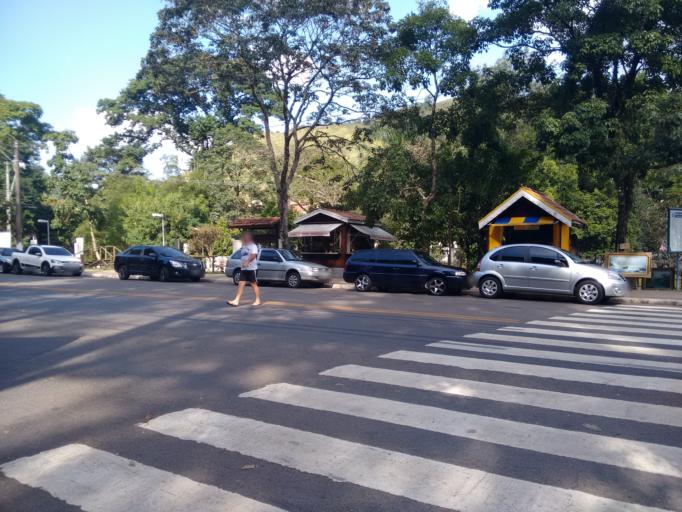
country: BR
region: Sao Paulo
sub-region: Sao Joao Da Boa Vista
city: Sao Joao da Boa Vista
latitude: -21.9338
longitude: -46.7158
